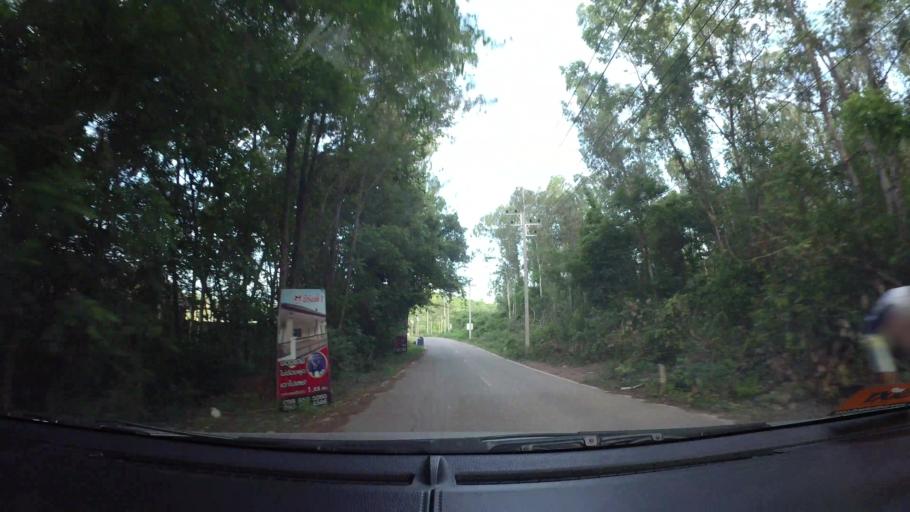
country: TH
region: Chon Buri
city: Sattahip
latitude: 12.7530
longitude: 100.9509
